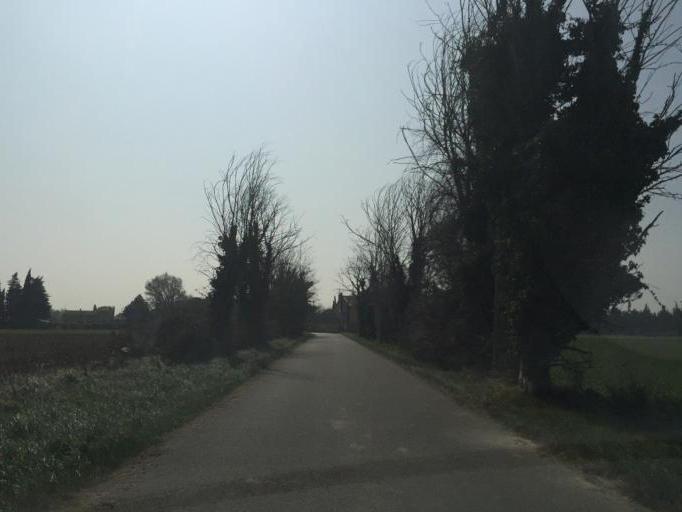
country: FR
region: Provence-Alpes-Cote d'Azur
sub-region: Departement du Vaucluse
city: Jonquieres
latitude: 44.1083
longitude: 4.8984
